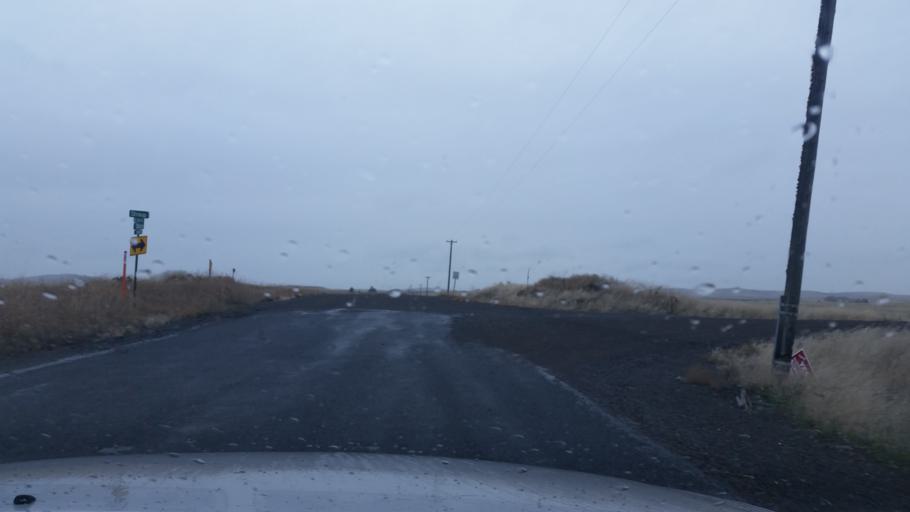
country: US
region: Washington
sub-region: Spokane County
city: Medical Lake
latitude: 47.6146
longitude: -117.7976
